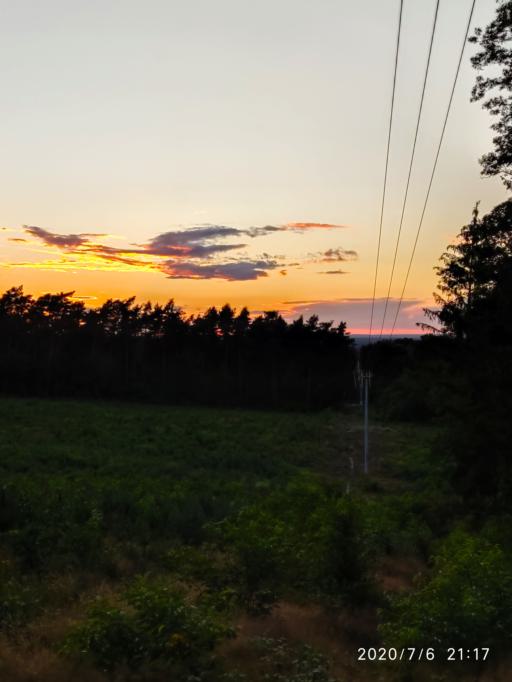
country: PL
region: Lubusz
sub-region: Zielona Gora
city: Zielona Gora
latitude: 51.9246
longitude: 15.4633
